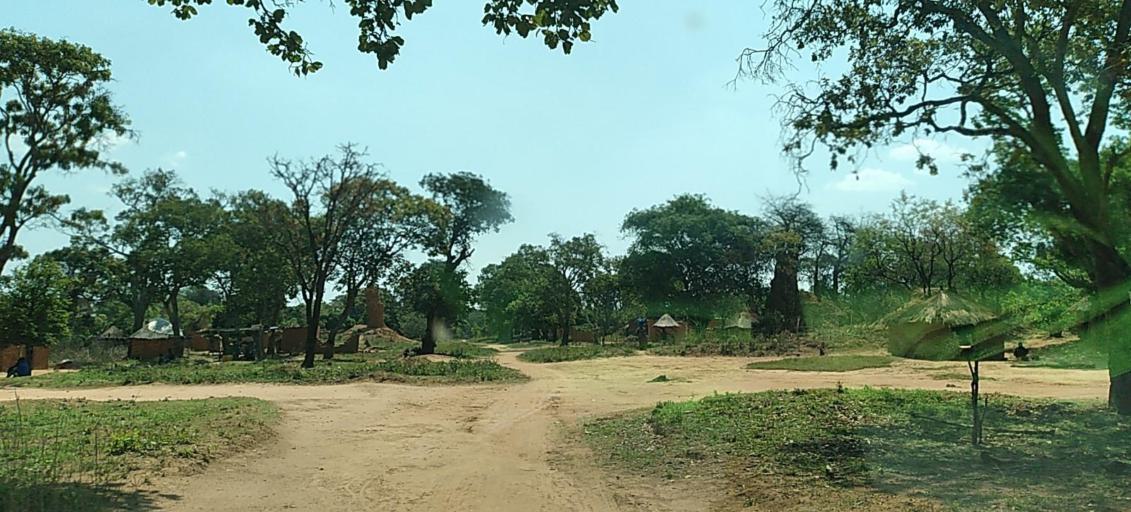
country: CD
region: Katanga
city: Kolwezi
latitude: -11.2790
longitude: 25.1308
